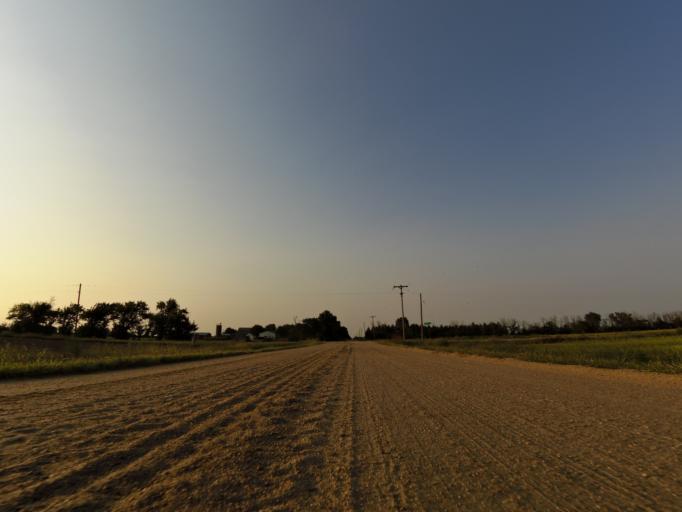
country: US
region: Kansas
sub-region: Reno County
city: South Hutchinson
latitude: 37.9841
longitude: -97.9959
